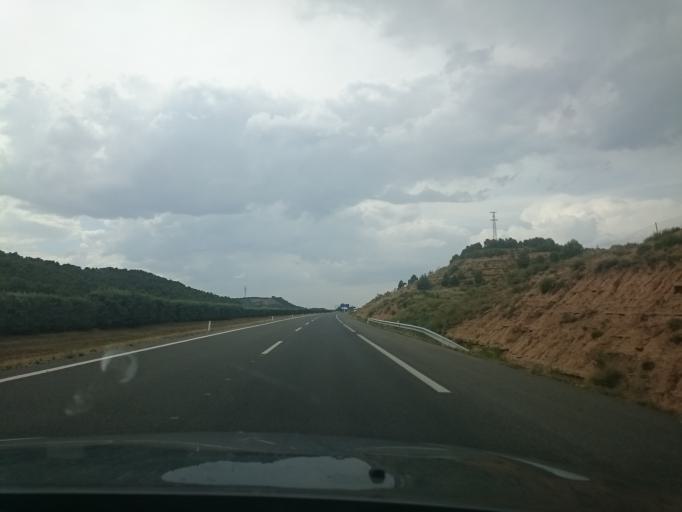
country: ES
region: Navarre
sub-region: Provincia de Navarra
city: Murchante
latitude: 42.0800
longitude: -1.7055
